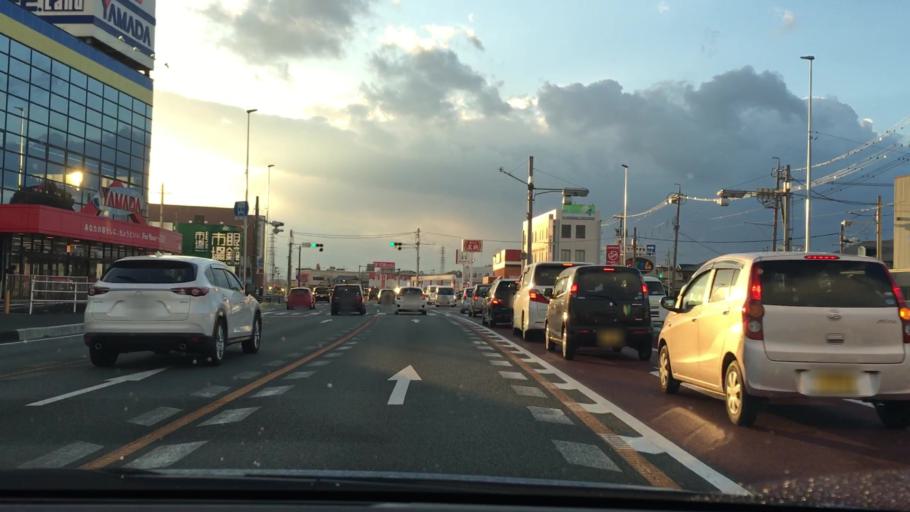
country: JP
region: Mie
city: Ise
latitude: 34.5089
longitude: 136.7218
